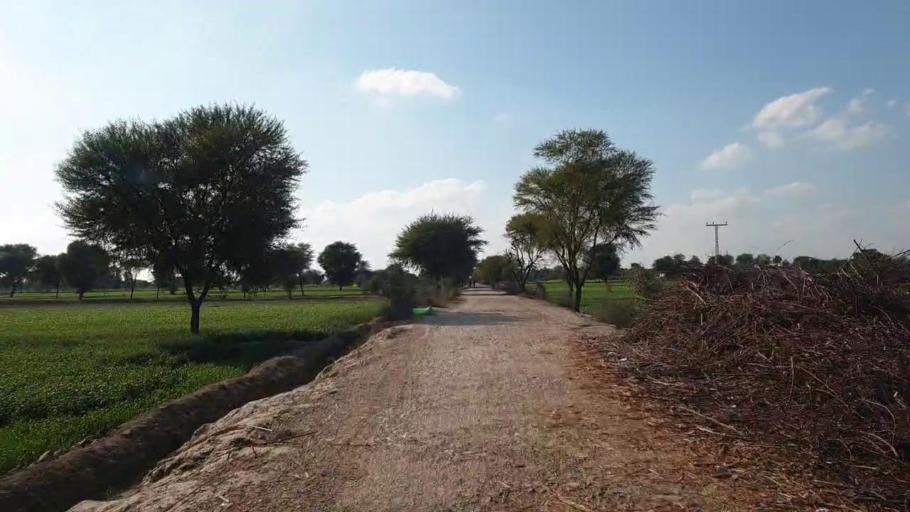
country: PK
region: Sindh
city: Shahpur Chakar
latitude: 26.1095
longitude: 68.5597
